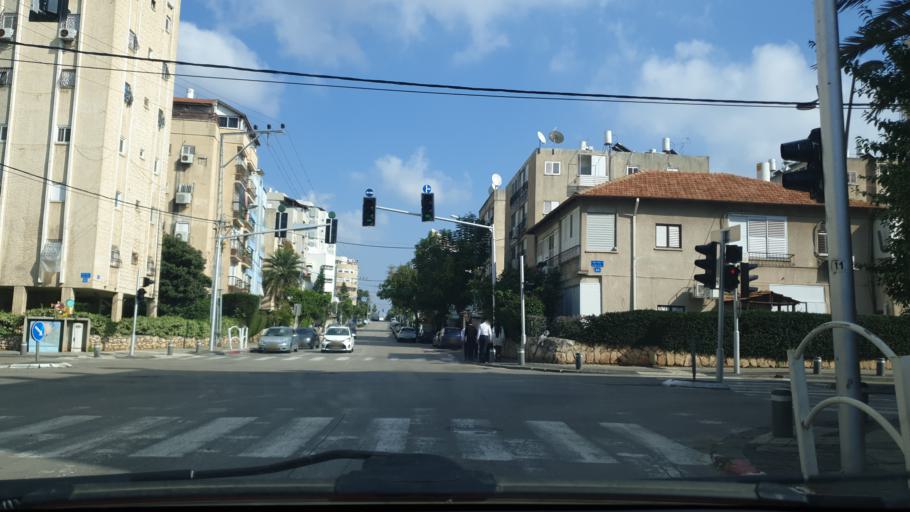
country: IL
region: Central District
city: Rishon LeZiyyon
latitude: 31.9669
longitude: 34.8099
